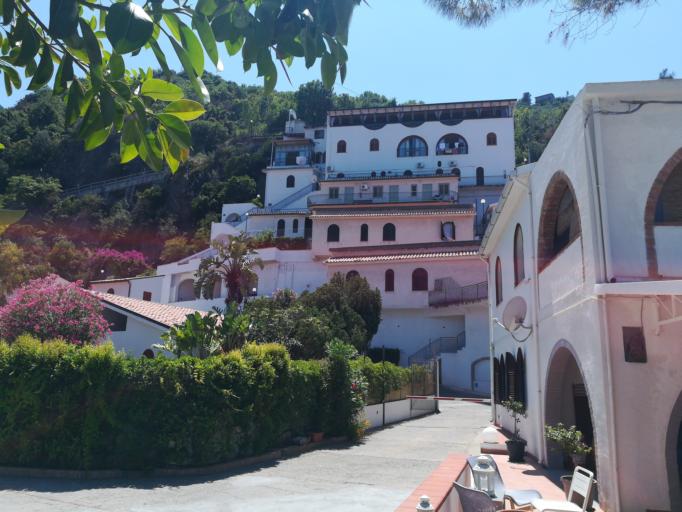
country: IT
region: Sicily
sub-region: Messina
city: Naso
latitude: 38.1530
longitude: 14.7827
